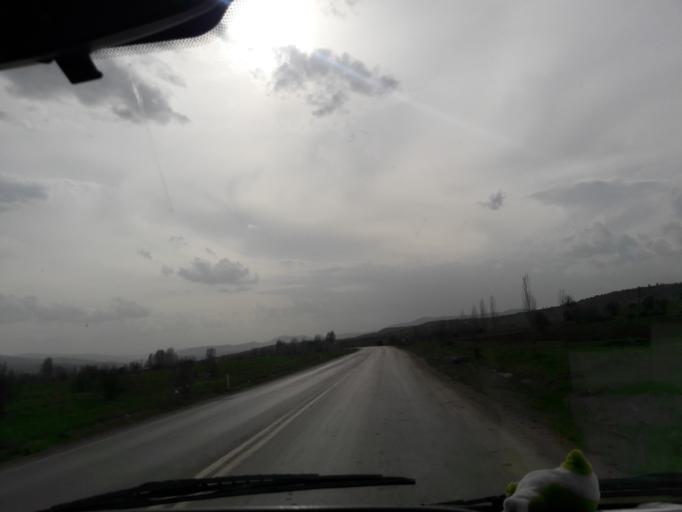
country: TR
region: Gumushane
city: Siran
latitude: 40.1774
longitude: 39.0990
